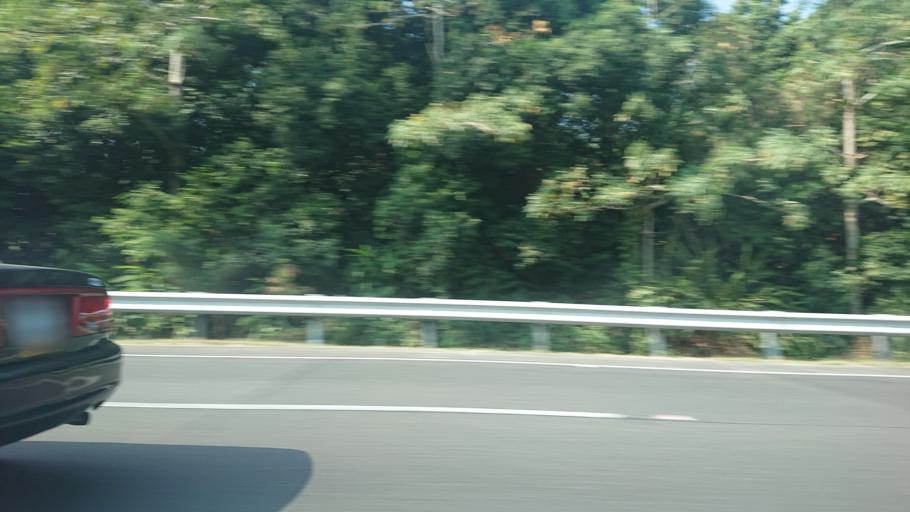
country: TW
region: Taiwan
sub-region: Nantou
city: Nantou
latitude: 23.8428
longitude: 120.7050
